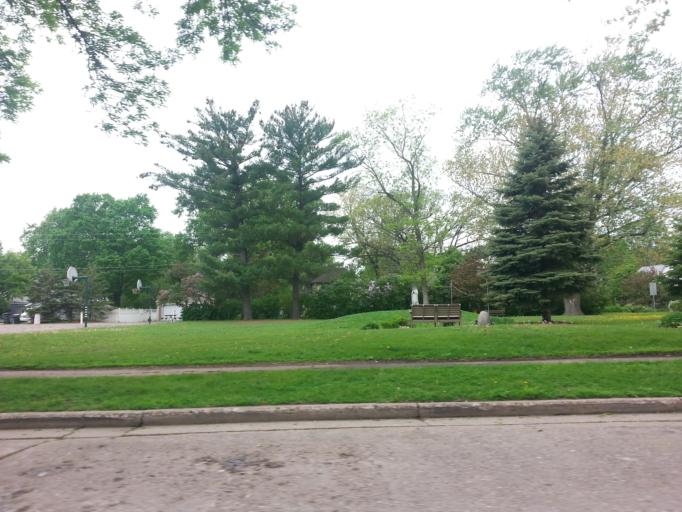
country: US
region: Wisconsin
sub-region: Saint Croix County
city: Hudson
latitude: 44.9834
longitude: -92.7541
